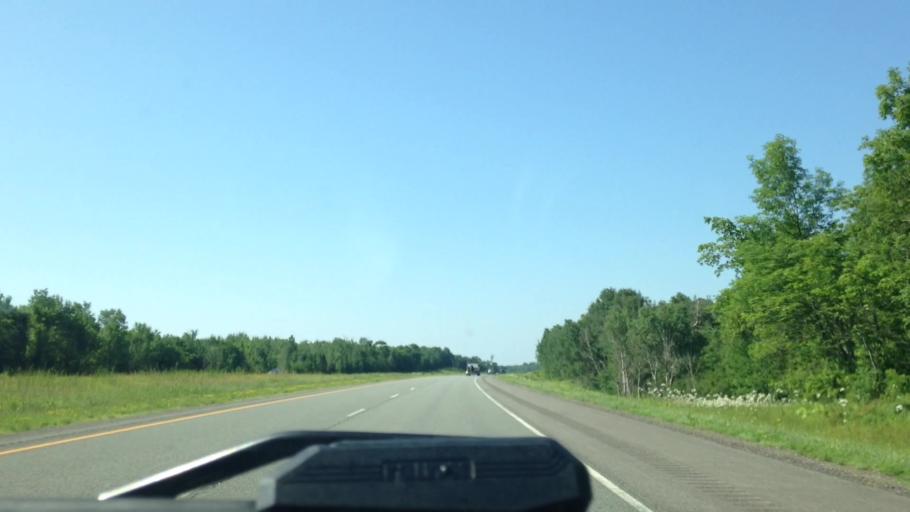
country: US
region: Wisconsin
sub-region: Douglas County
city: Lake Nebagamon
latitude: 46.4109
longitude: -91.8113
